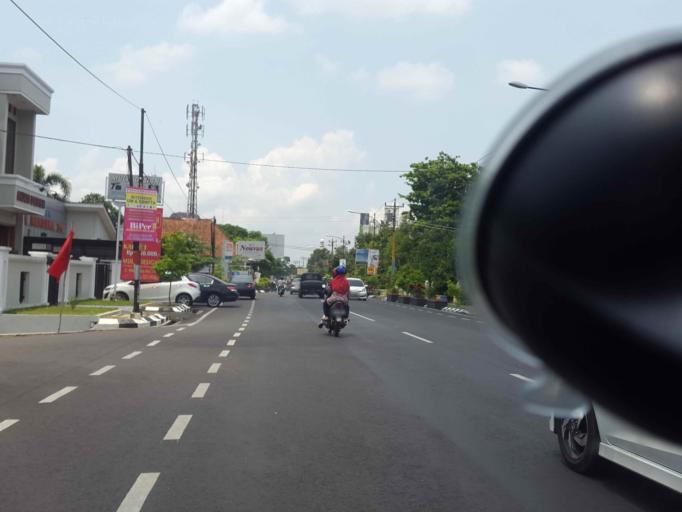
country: ID
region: Central Java
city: Purwokerto
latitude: -7.4224
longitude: 109.2376
